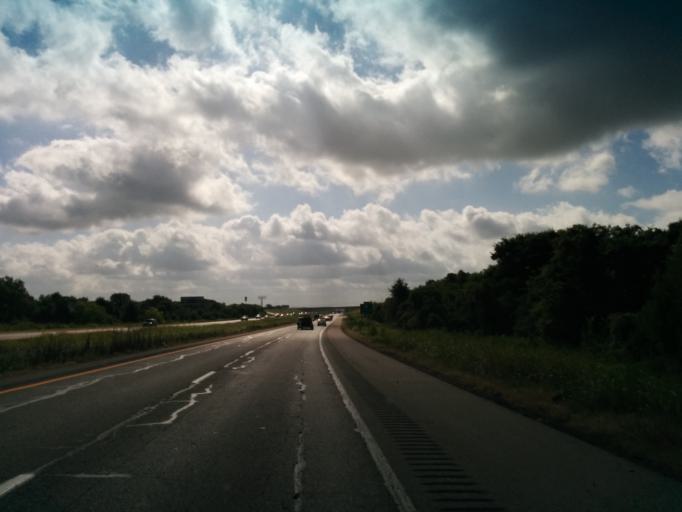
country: US
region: Texas
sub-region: Caldwell County
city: Luling
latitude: 29.6517
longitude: -97.6692
